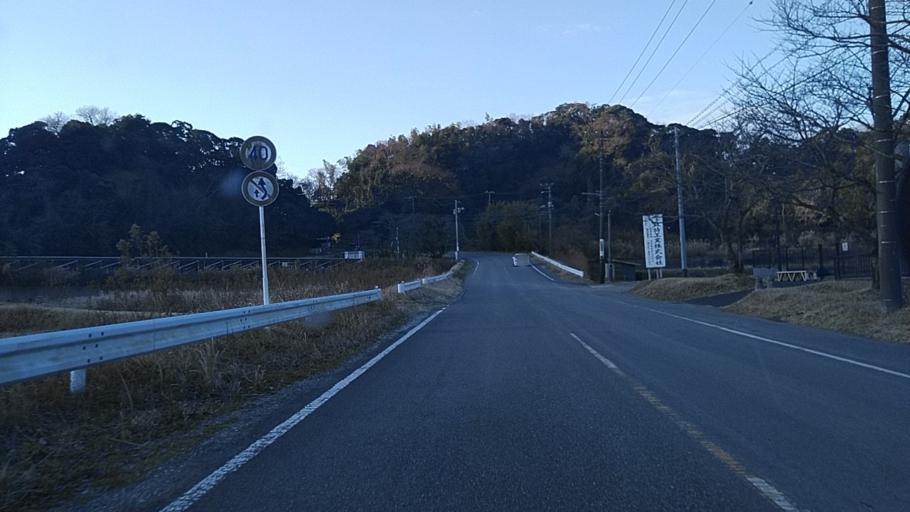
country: JP
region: Chiba
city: Kimitsu
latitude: 35.2724
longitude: 139.9207
